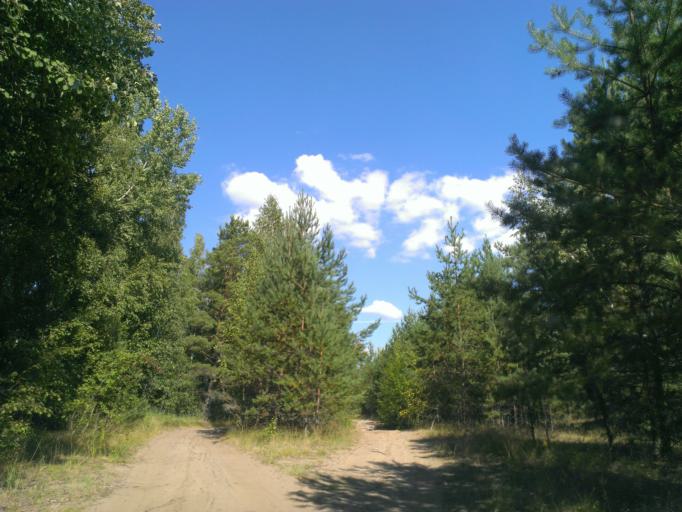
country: LV
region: Adazi
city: Adazi
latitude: 57.1113
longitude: 24.3565
